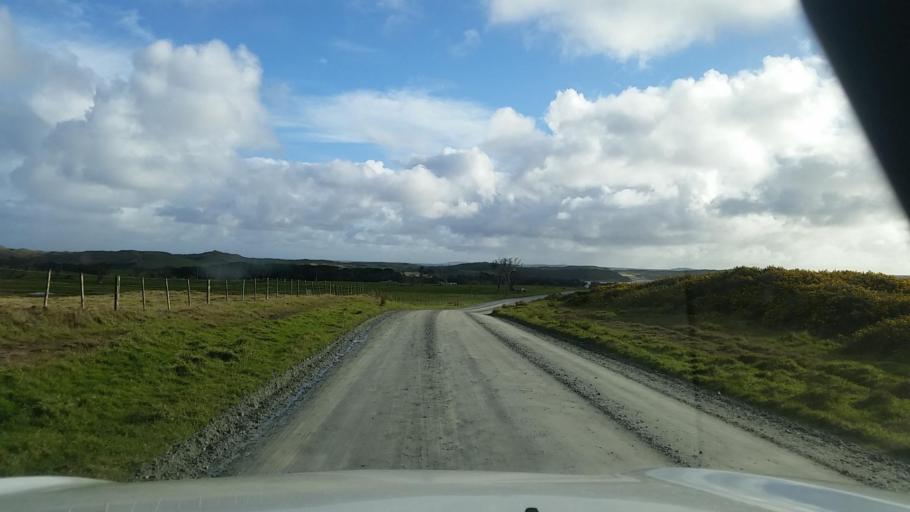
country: NZ
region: Chatham Islands
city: Waitangi
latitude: -43.8315
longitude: -176.5483
